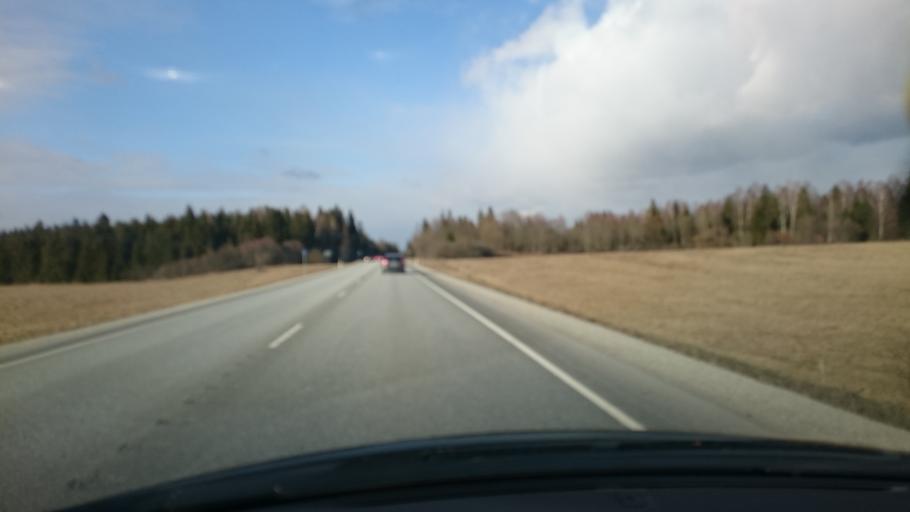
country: EE
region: Harju
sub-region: Keila linn
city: Keila
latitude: 59.2166
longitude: 24.4350
